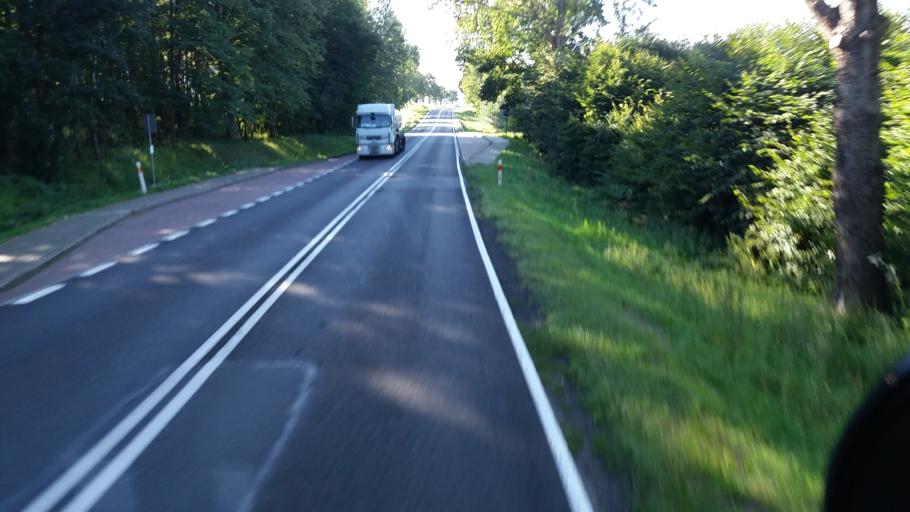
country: PL
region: West Pomeranian Voivodeship
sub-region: Powiat drawski
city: Kalisz Pomorski
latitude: 53.2898
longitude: 15.9444
